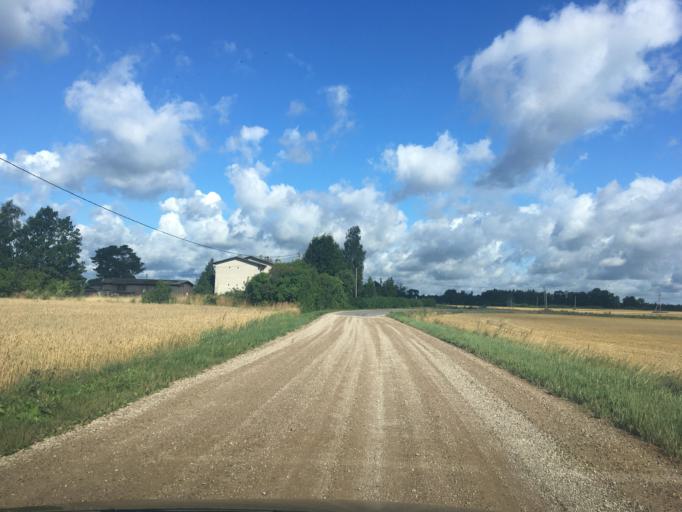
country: EE
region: Jogevamaa
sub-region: Poltsamaa linn
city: Poltsamaa
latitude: 58.4659
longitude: 25.9528
